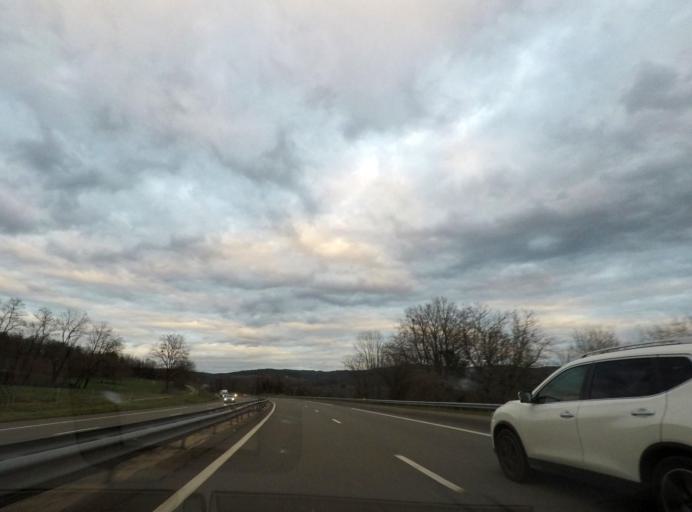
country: FR
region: Rhone-Alpes
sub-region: Departement de l'Ain
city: Neuville-sur-Ain
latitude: 46.0869
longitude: 5.3925
